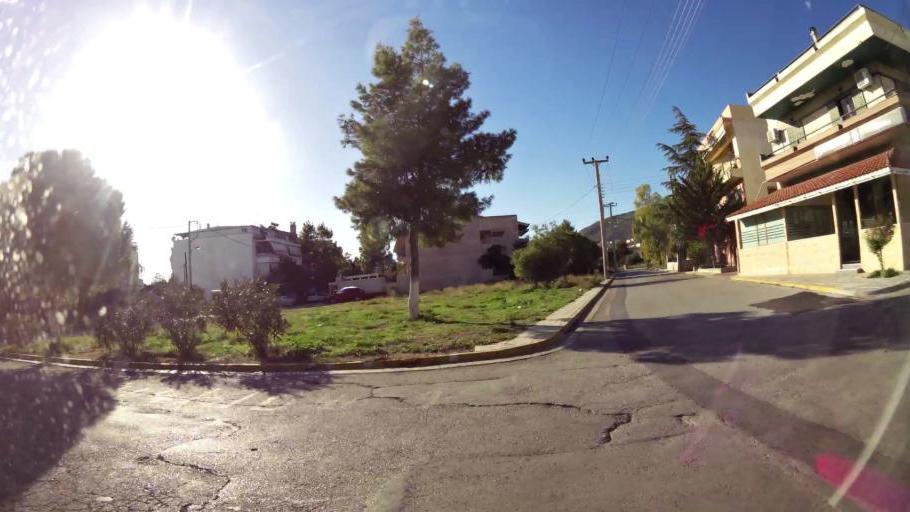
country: GR
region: Attica
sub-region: Nomarchia Anatolikis Attikis
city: Acharnes
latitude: 38.0970
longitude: 23.7283
